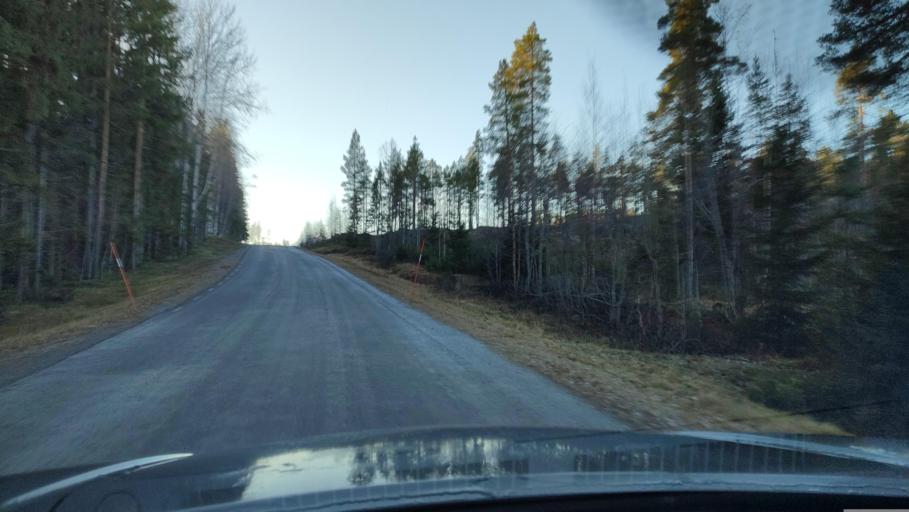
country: SE
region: Vaesterbotten
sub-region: Skelleftea Kommun
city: Viken
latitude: 64.7121
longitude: 20.9077
